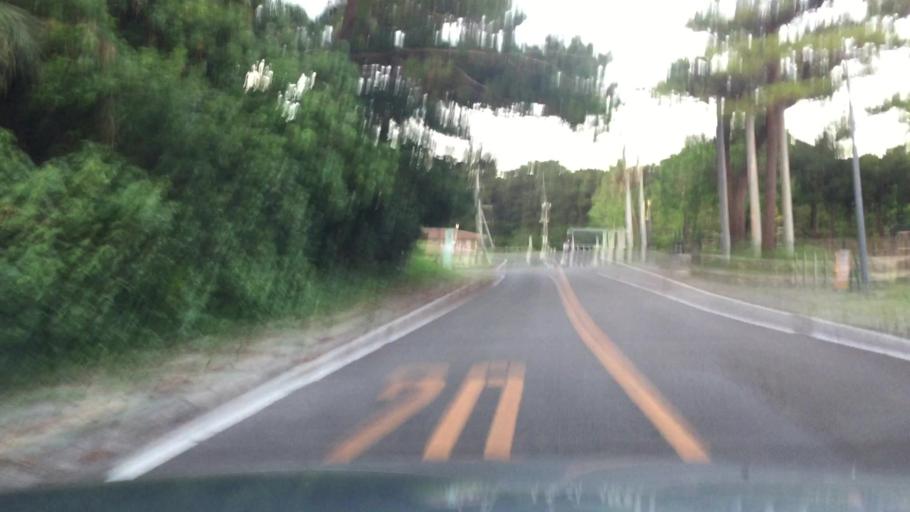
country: JP
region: Okinawa
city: Ishigaki
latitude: 24.3686
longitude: 124.1577
